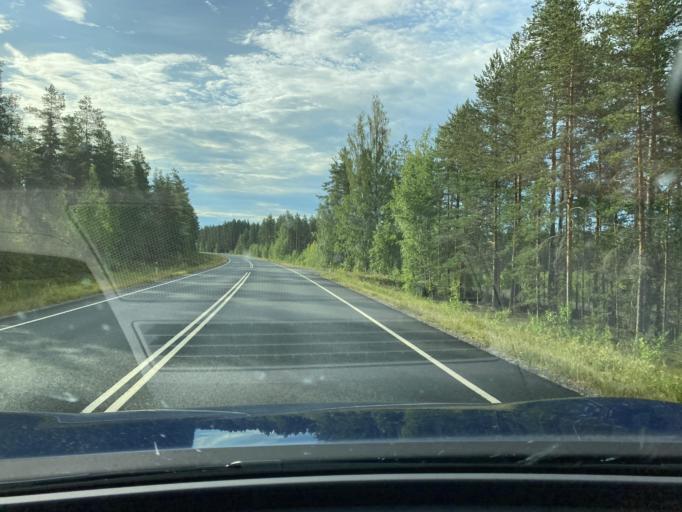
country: FI
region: Central Ostrobothnia
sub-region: Kaustinen
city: Veteli
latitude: 63.4116
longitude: 23.9566
